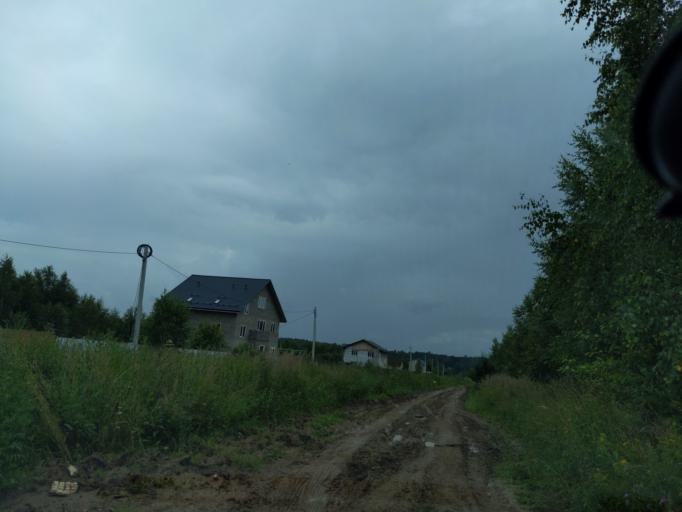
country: RU
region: Moskovskaya
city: Lugovaya
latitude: 56.0587
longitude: 37.4995
